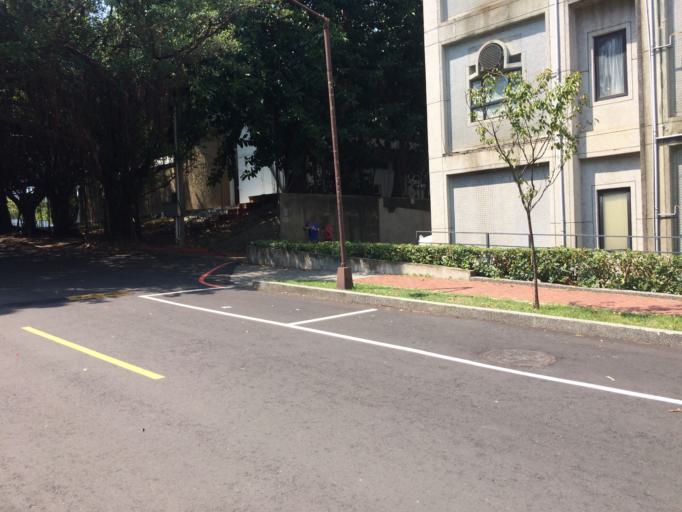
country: TW
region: Taiwan
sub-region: Hsinchu
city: Hsinchu
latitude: 24.7940
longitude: 120.9921
